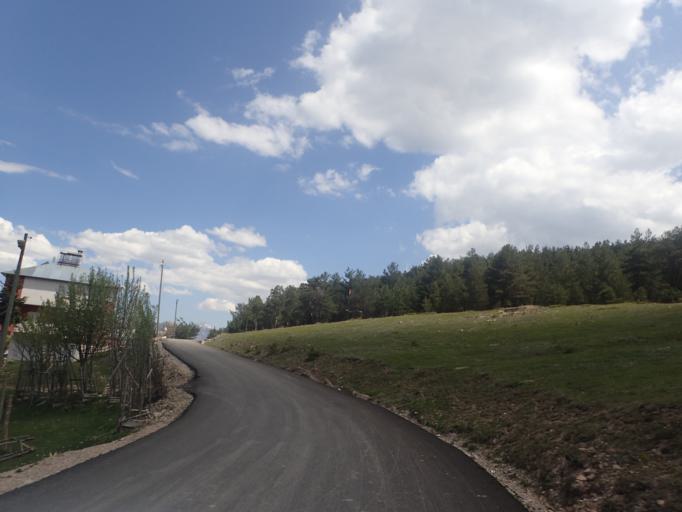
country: TR
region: Ordu
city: Mesudiye
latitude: 40.4050
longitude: 37.8608
